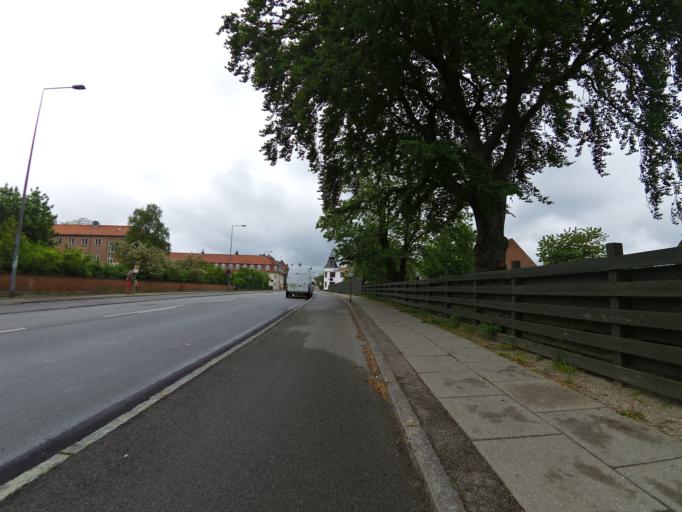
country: DK
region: Capital Region
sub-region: Gladsaxe Municipality
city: Buddinge
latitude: 55.7288
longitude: 12.5194
